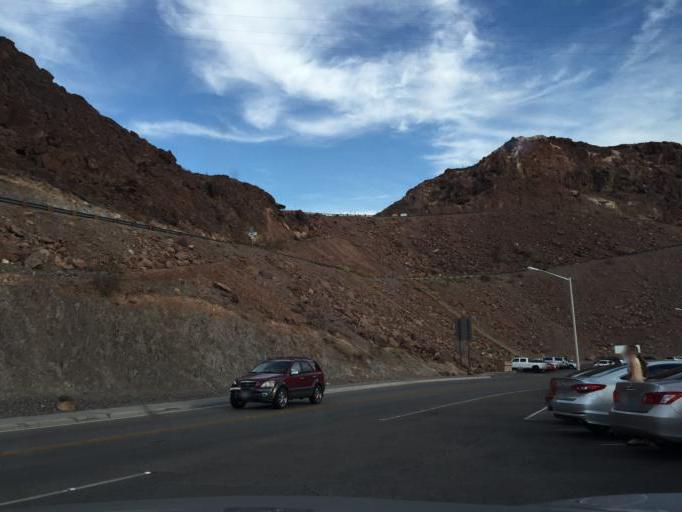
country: US
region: Nevada
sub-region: Clark County
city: Boulder City
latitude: 36.0153
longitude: -114.7338
